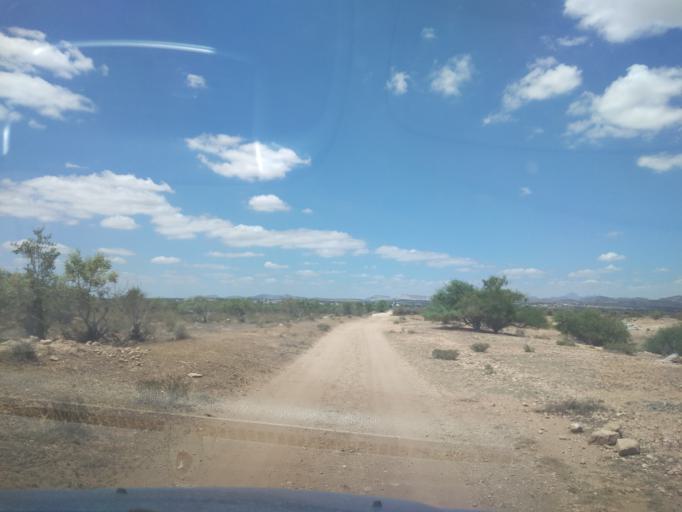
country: TN
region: Susah
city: Harqalah
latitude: 36.1660
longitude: 10.4435
